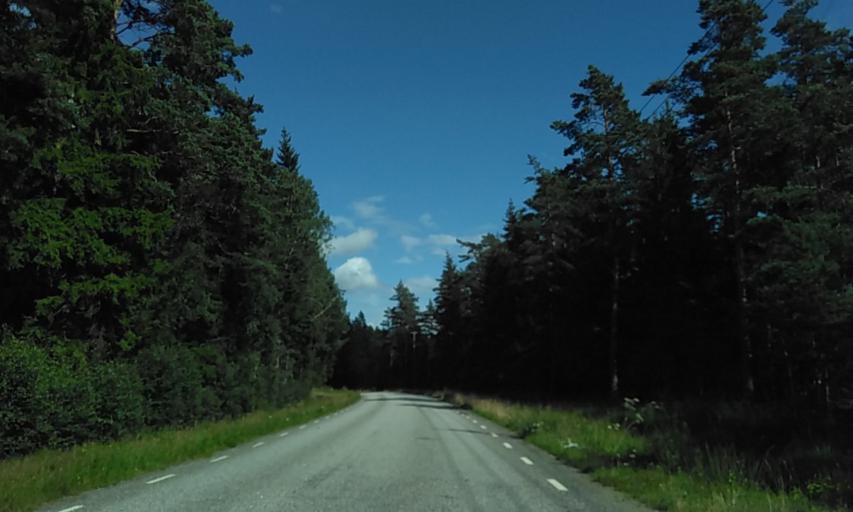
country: SE
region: Vaestra Goetaland
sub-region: Vargarda Kommun
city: Jonstorp
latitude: 57.9376
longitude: 12.7531
